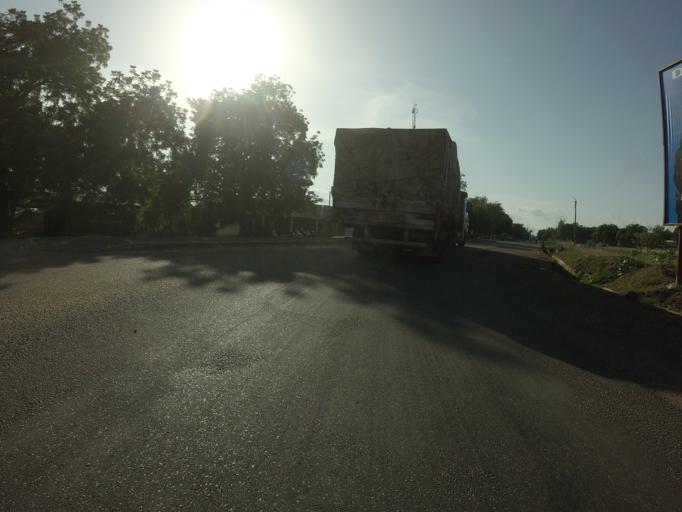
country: GH
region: Upper East
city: Navrongo
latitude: 10.8963
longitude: -1.0914
